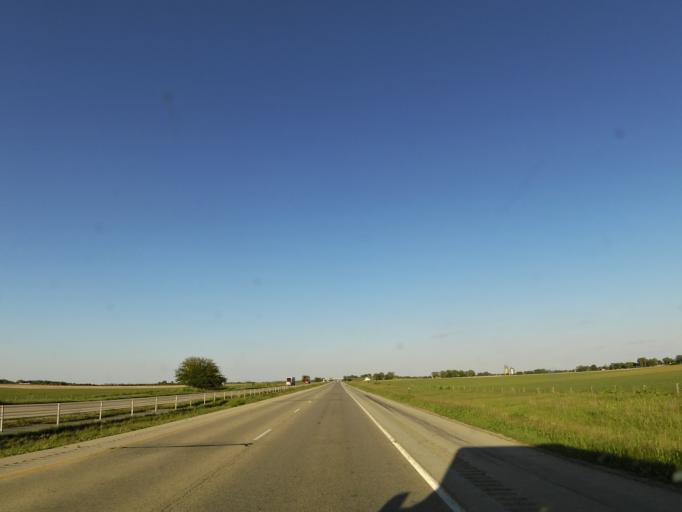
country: US
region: Illinois
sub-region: Champaign County
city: Saint Joseph
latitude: 40.1204
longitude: -88.1208
